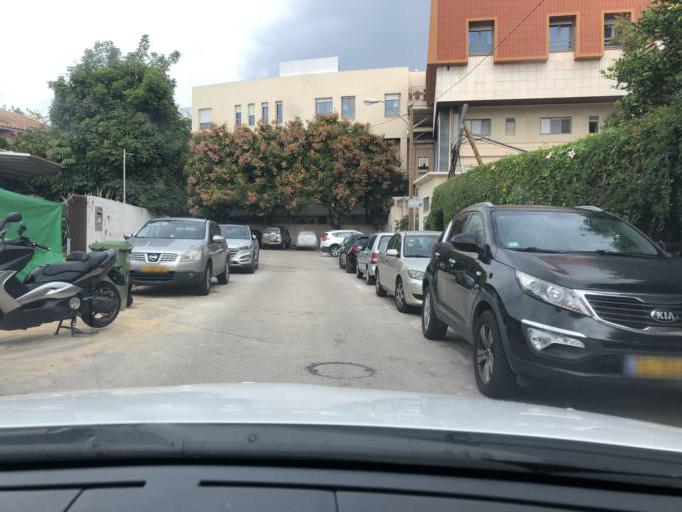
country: IL
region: Tel Aviv
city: Giv`atayim
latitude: 32.0548
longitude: 34.8220
